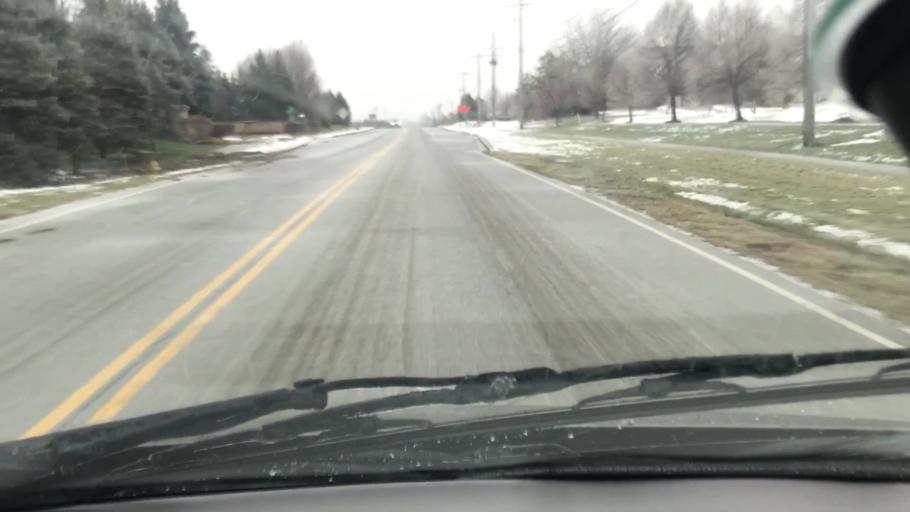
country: US
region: Indiana
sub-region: Hamilton County
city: Carmel
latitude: 39.9712
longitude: -86.0747
